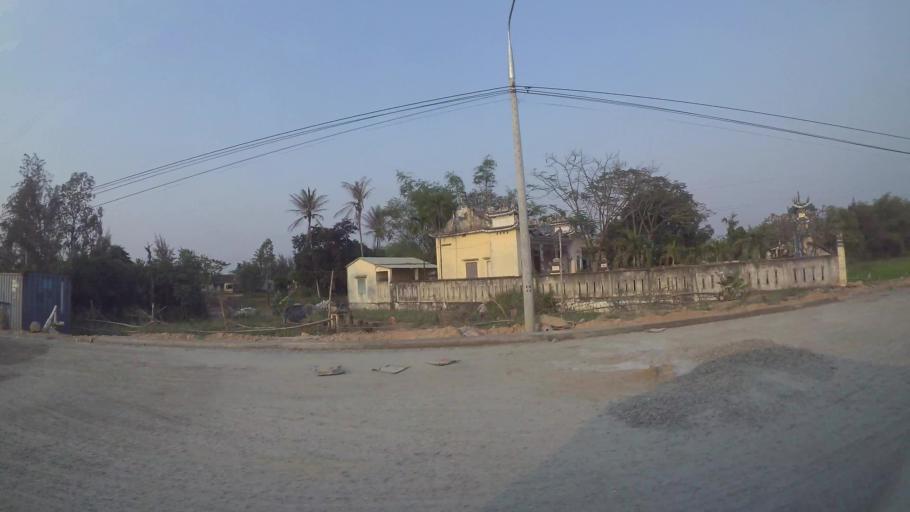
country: VN
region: Da Nang
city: Ngu Hanh Son
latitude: 15.9579
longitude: 108.2340
